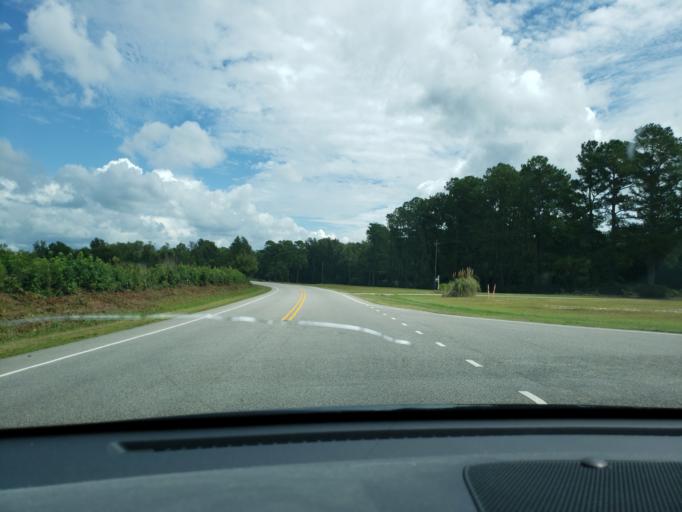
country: US
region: North Carolina
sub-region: Columbus County
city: Tabor City
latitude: 34.1885
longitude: -78.7757
